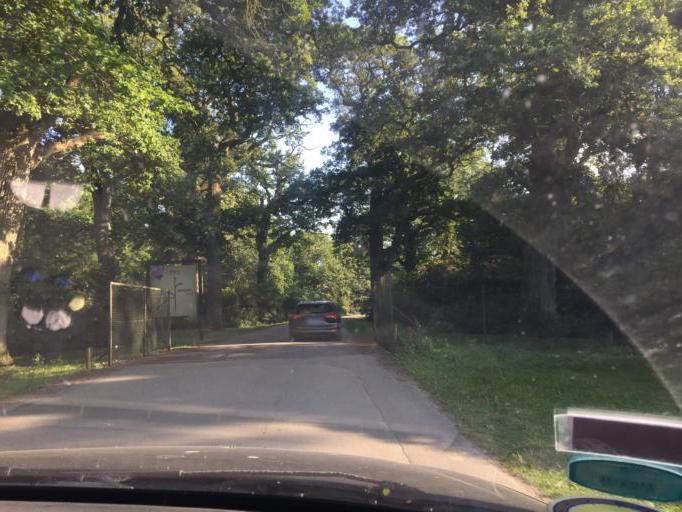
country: DK
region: Zealand
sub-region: Lolland Kommune
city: Maribo
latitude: 54.8133
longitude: 11.5110
